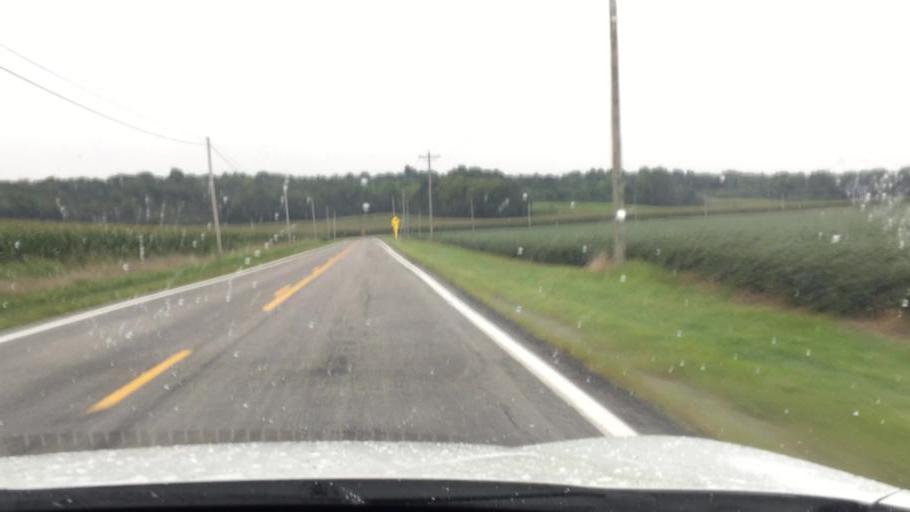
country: US
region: Ohio
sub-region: Champaign County
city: Mechanicsburg
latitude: 40.0283
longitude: -83.6438
